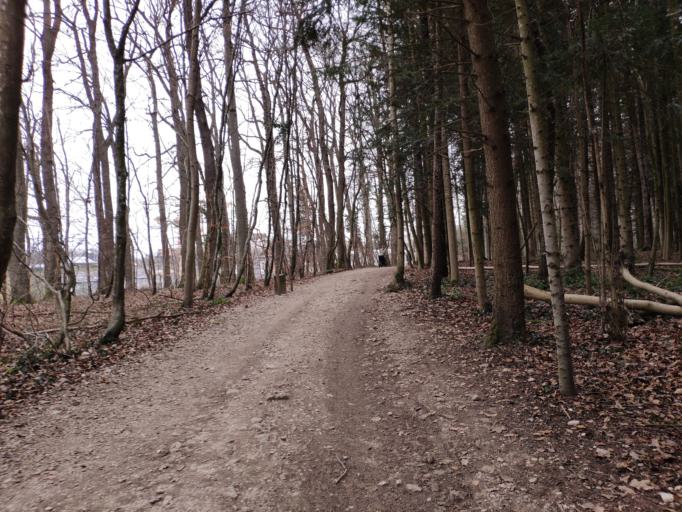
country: CH
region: Basel-City
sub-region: Basel-Stadt
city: Bettingen
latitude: 47.5689
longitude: 7.6784
